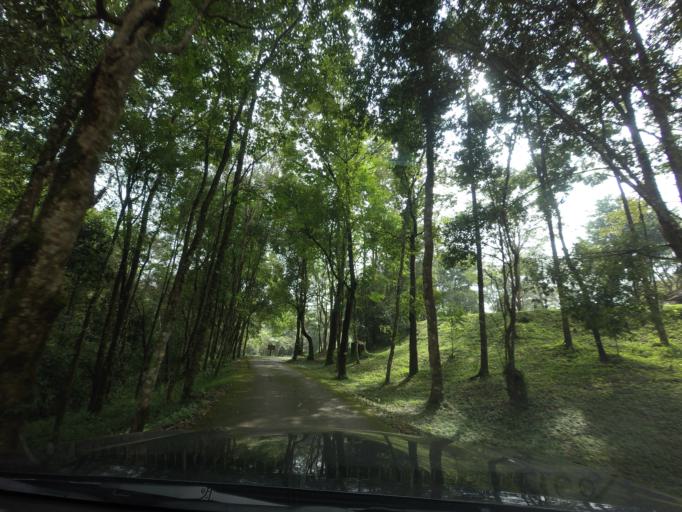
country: TH
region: Nan
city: Bo Kluea
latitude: 19.2046
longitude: 101.0780
